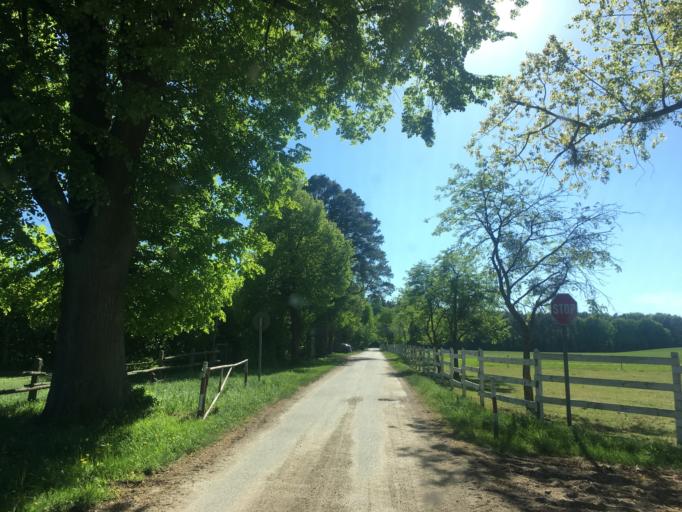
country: PL
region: Warmian-Masurian Voivodeship
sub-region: Powiat mragowski
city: Mikolajki
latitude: 53.7503
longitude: 21.6250
